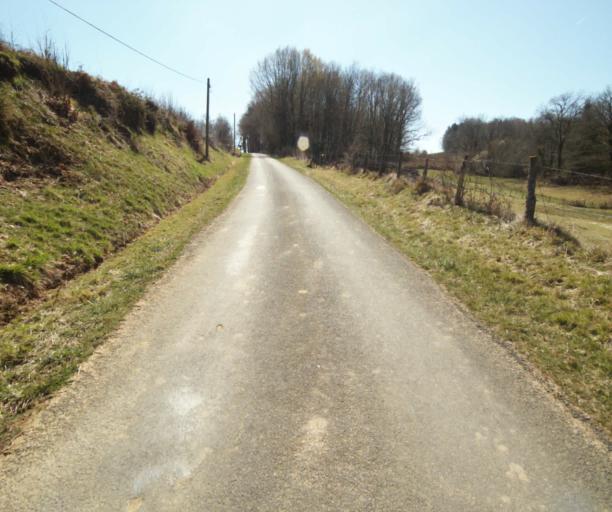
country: FR
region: Limousin
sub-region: Departement de la Correze
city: Saint-Clement
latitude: 45.3169
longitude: 1.6962
